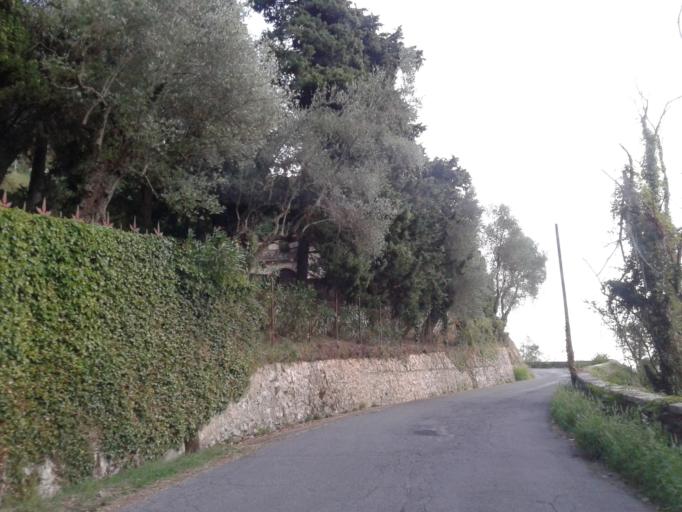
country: IT
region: Tuscany
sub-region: Provincia di Lucca
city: Pontestazzemese
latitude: 43.9558
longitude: 10.3089
